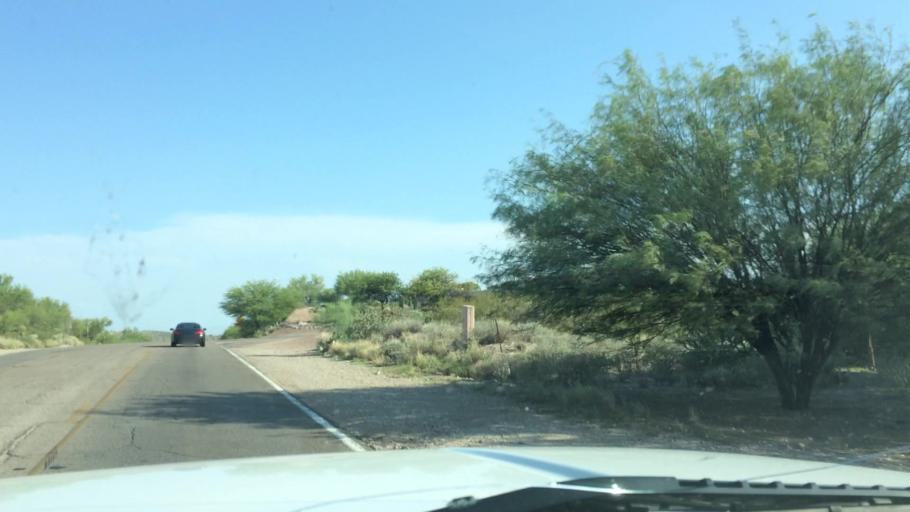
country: US
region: Arizona
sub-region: Pima County
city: Catalina Foothills
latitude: 32.3055
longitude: -110.8432
